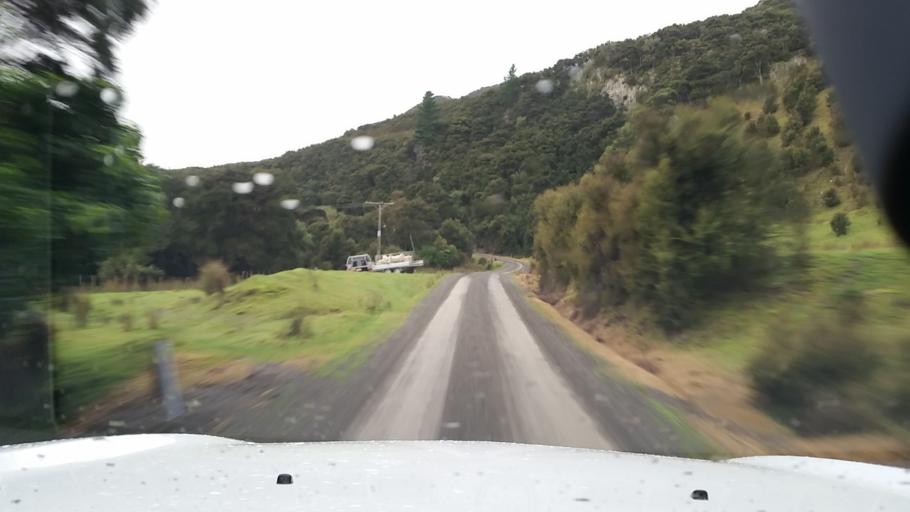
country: NZ
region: Wellington
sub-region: South Wairarapa District
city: Waipawa
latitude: -41.3516
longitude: 175.6844
